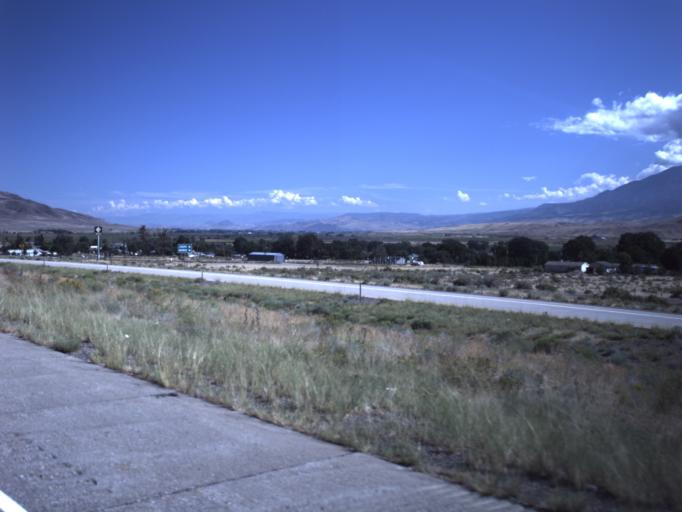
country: US
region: Utah
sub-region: Sevier County
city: Monroe
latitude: 38.6211
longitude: -112.2275
